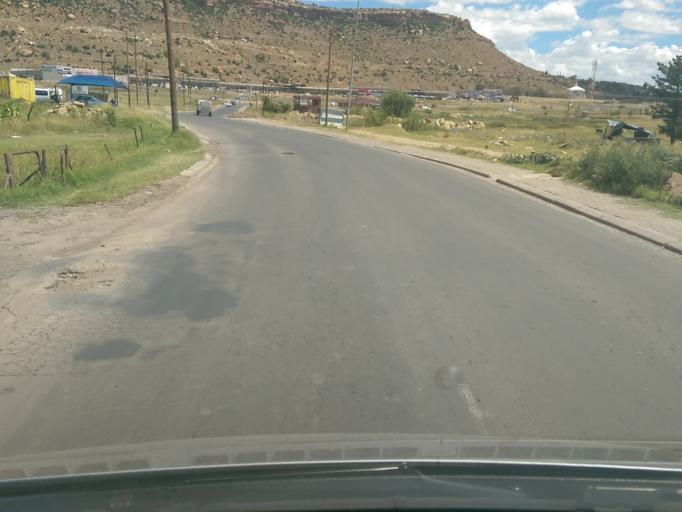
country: LS
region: Maseru
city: Maseru
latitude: -29.3300
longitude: 27.4862
